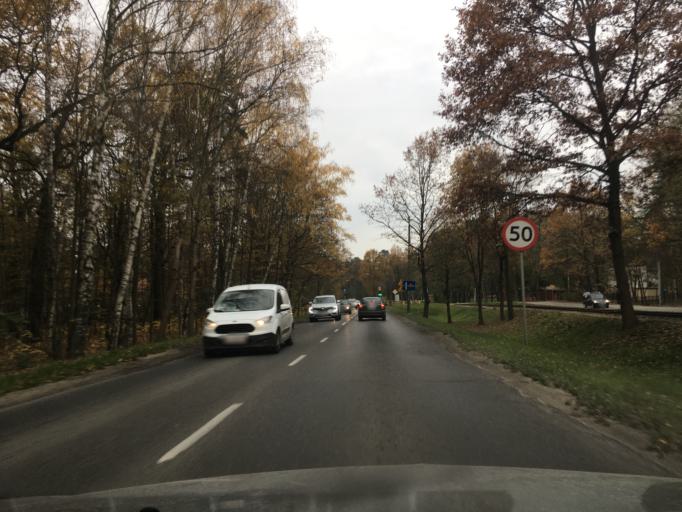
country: PL
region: Masovian Voivodeship
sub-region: Powiat piaseczynski
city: Piaseczno
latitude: 52.0611
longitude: 21.0120
